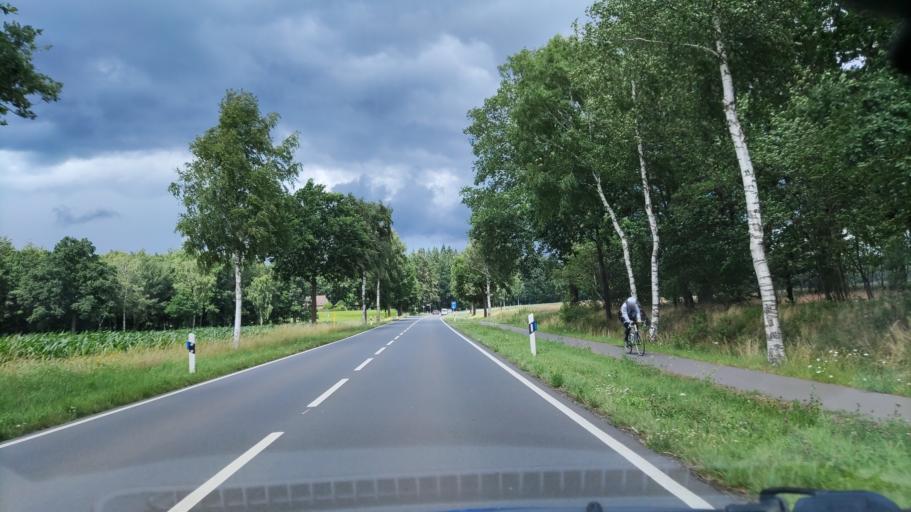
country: DE
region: Lower Saxony
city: Soltau
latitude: 52.9626
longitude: 9.7975
